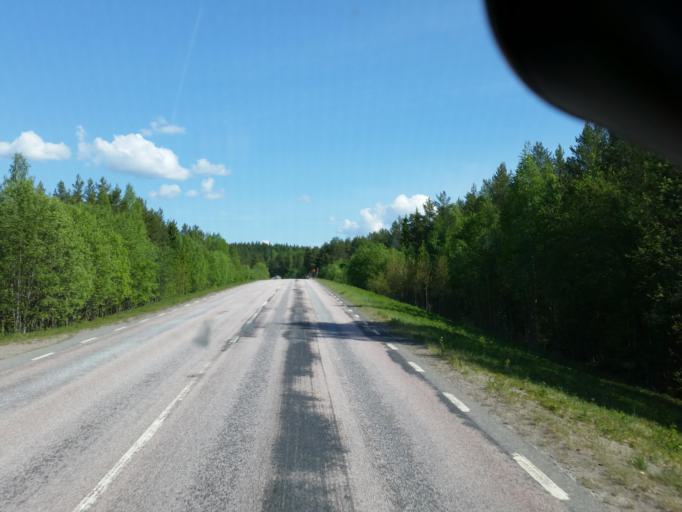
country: SE
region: Norrbotten
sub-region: Pitea Kommun
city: Roknas
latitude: 65.5311
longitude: 21.2151
